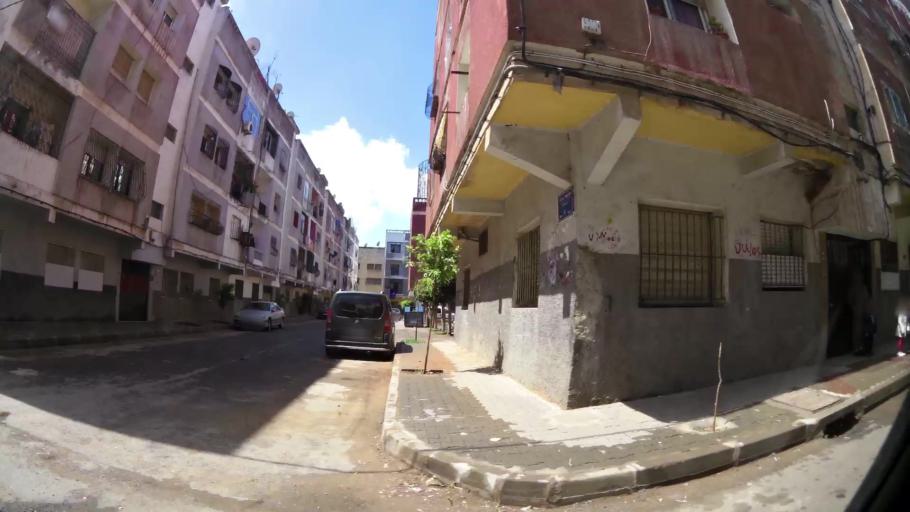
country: MA
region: Grand Casablanca
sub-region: Mediouna
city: Tit Mellil
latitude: 33.5408
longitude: -7.5512
